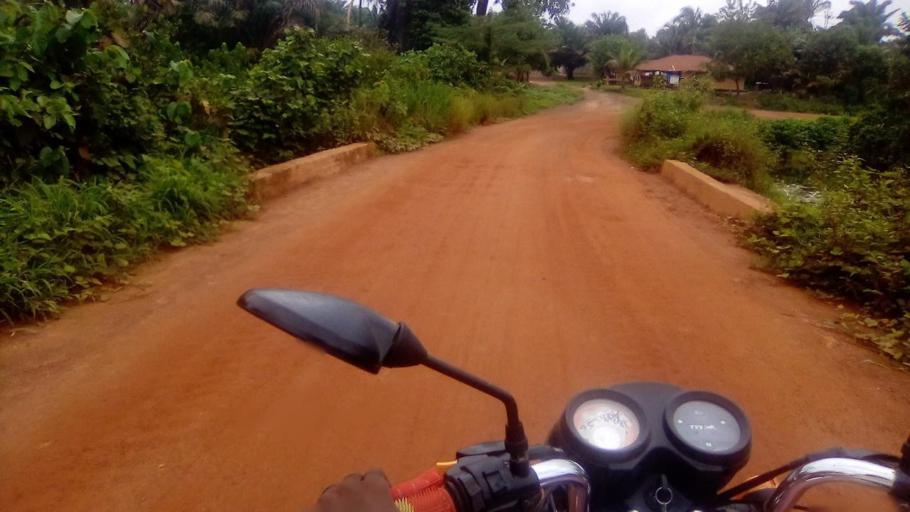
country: SL
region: Southern Province
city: Tongole
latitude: 7.4381
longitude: -11.8633
